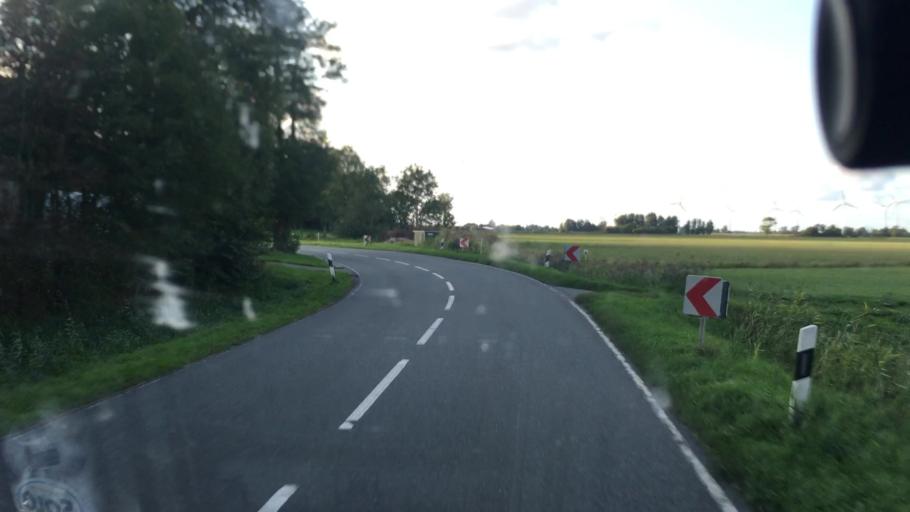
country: DE
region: Lower Saxony
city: Wittmund
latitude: 53.6409
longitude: 7.8181
